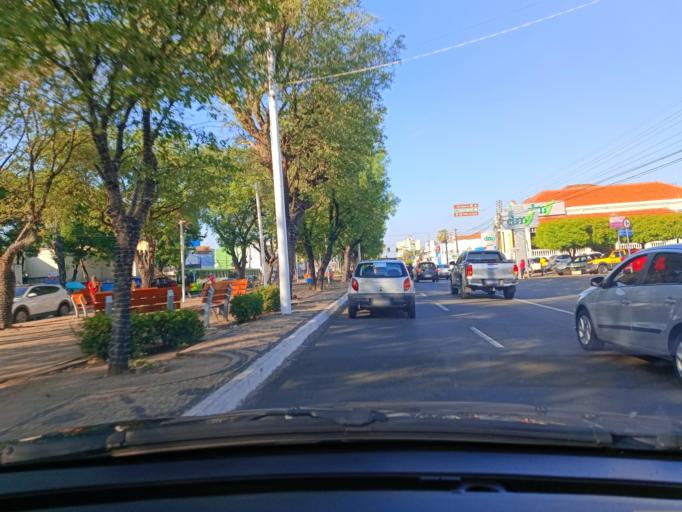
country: BR
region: Piaui
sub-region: Teresina
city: Teresina
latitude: -5.0873
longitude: -42.8047
